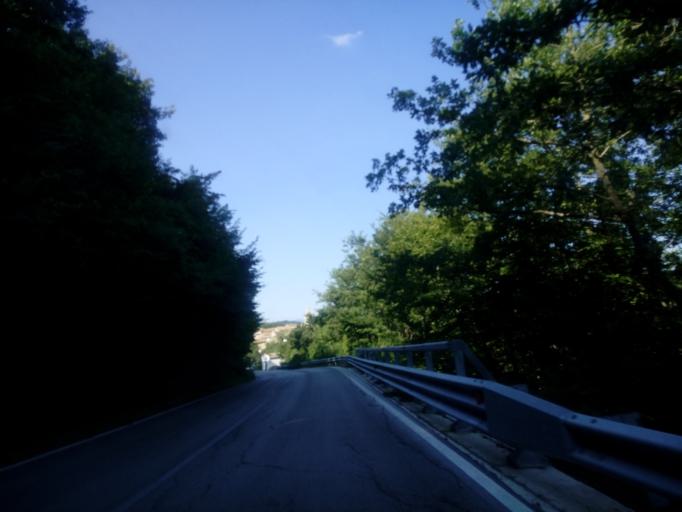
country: IT
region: Molise
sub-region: Provincia di Campobasso
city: Gildone
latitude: 41.5122
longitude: 14.7434
